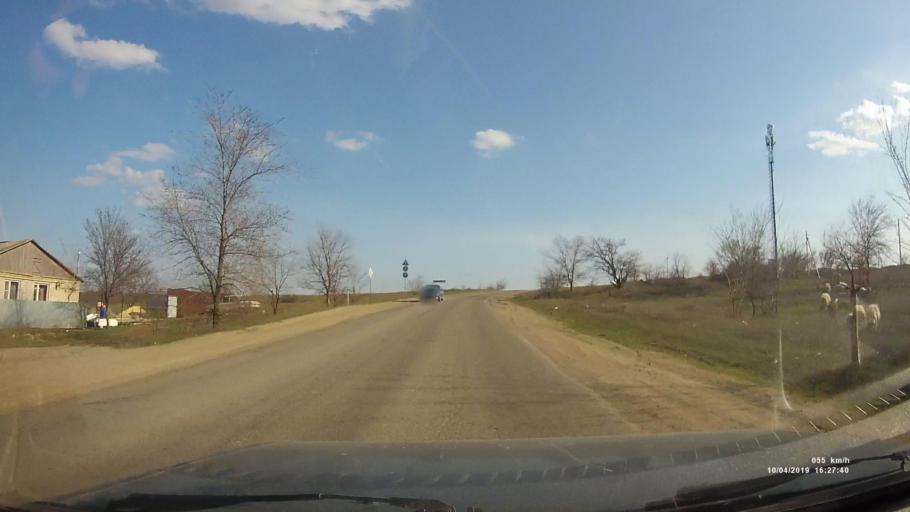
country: RU
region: Rostov
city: Staraya Stanitsa
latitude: 48.2823
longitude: 40.3437
